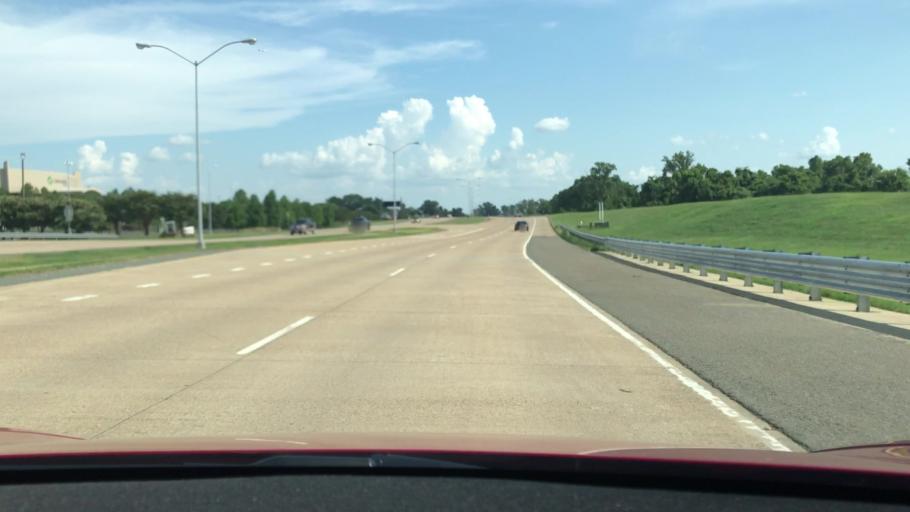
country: US
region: Louisiana
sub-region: Bossier Parish
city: Bossier City
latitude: 32.4687
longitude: -93.6775
